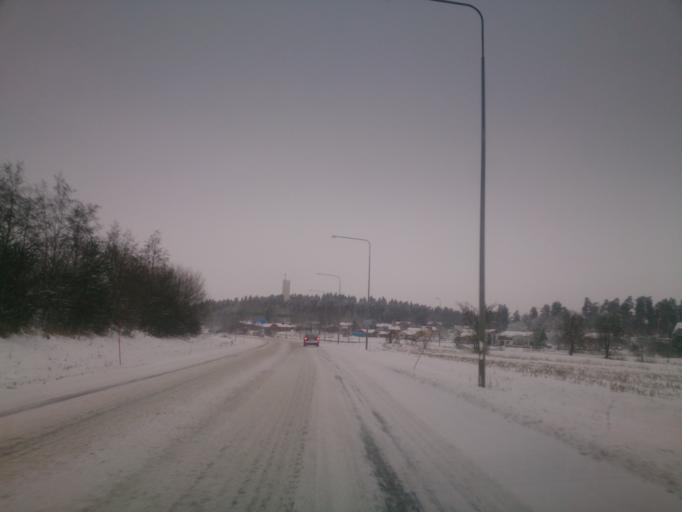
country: SE
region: OEstergoetland
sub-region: Norrkopings Kommun
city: Kimstad
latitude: 58.5391
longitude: 15.9773
